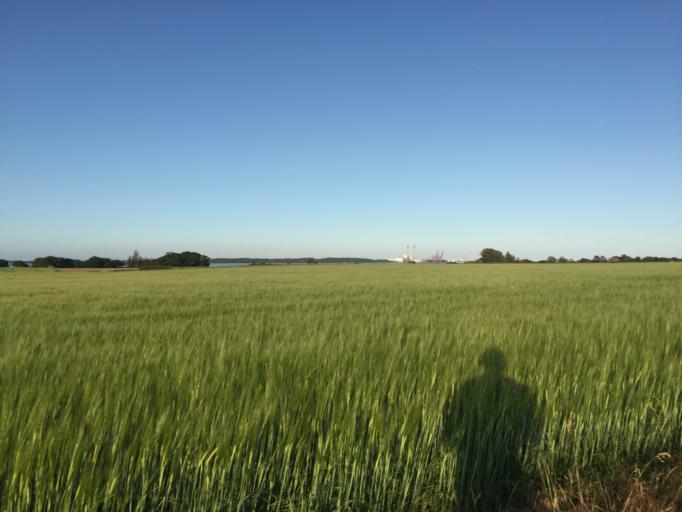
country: DK
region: Zealand
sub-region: Slagelse Kommune
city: Skaelskor
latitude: 55.2187
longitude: 11.1862
